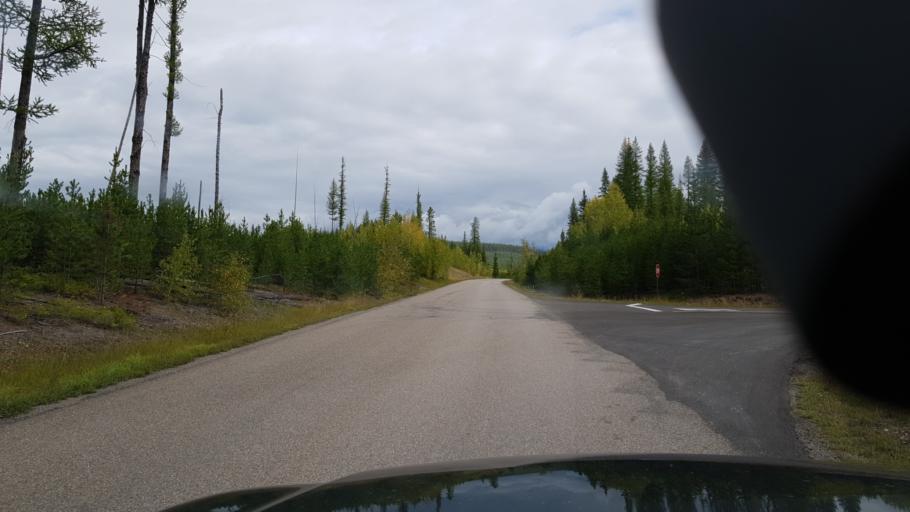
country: US
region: Montana
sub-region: Flathead County
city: Columbia Falls
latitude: 48.6233
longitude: -114.1325
